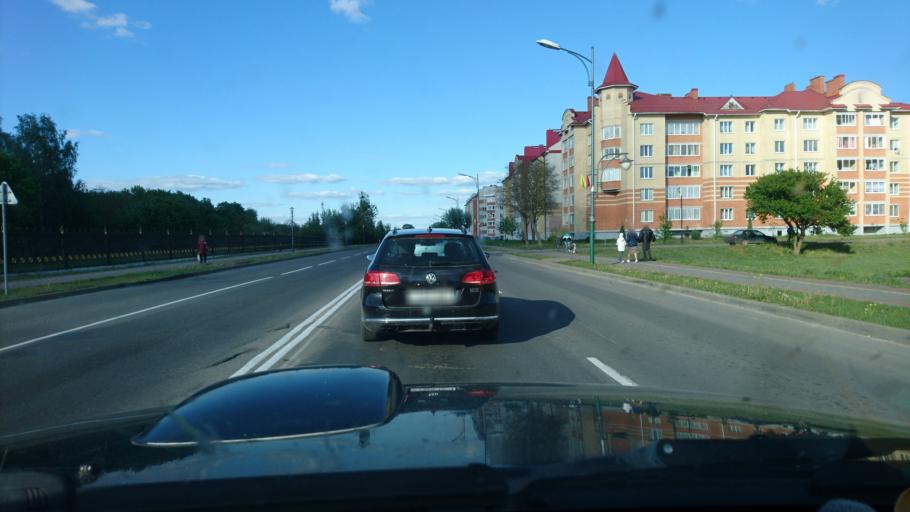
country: BY
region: Brest
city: Byaroza
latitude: 52.5366
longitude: 24.9892
